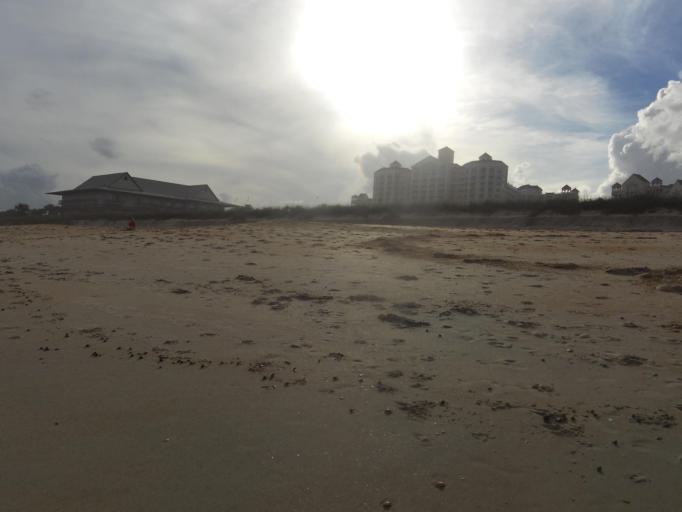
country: US
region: Florida
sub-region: Flagler County
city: Palm Coast
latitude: 29.6073
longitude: -81.1861
